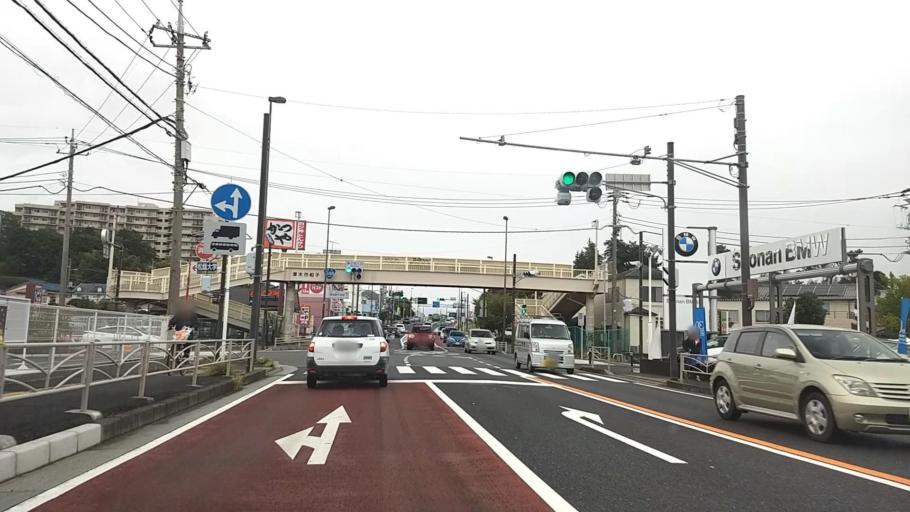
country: JP
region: Kanagawa
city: Atsugi
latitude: 35.4260
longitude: 139.3504
